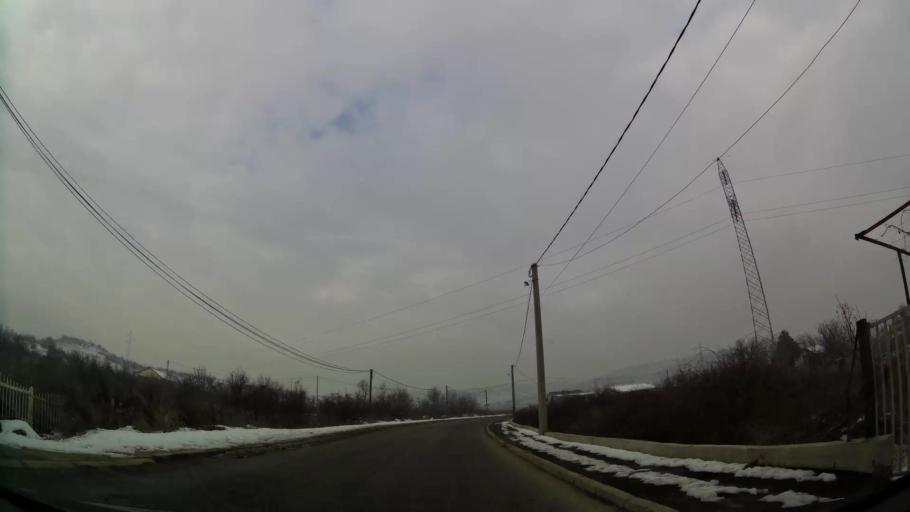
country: MK
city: Kondovo
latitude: 42.0364
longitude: 21.3399
